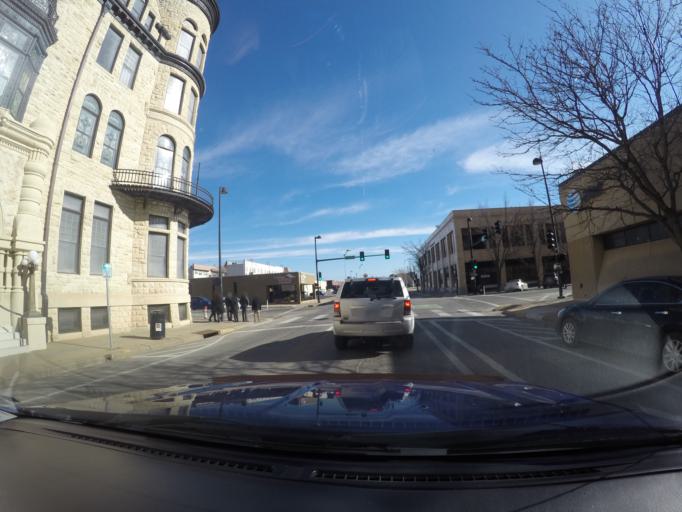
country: US
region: Kansas
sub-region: Sedgwick County
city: Wichita
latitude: 37.6880
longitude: -97.3346
